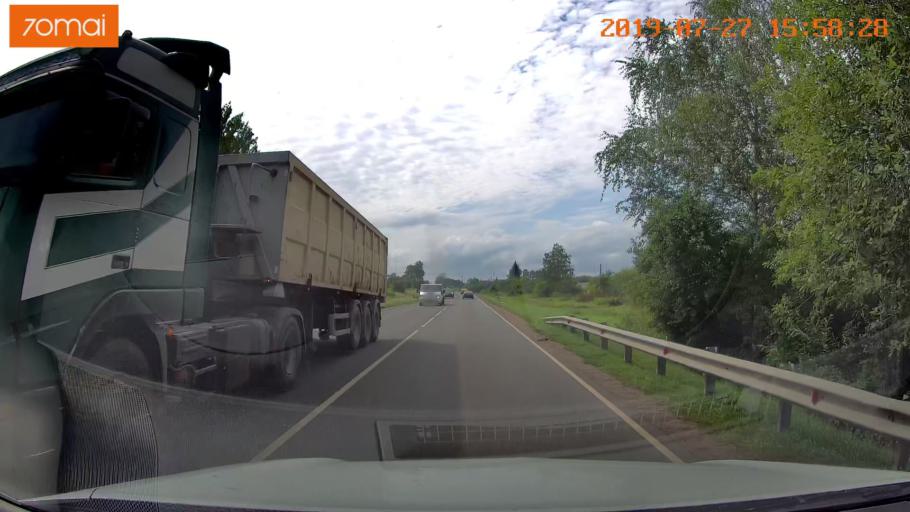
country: RU
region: Kaliningrad
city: Chernyakhovsk
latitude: 54.6261
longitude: 21.8639
